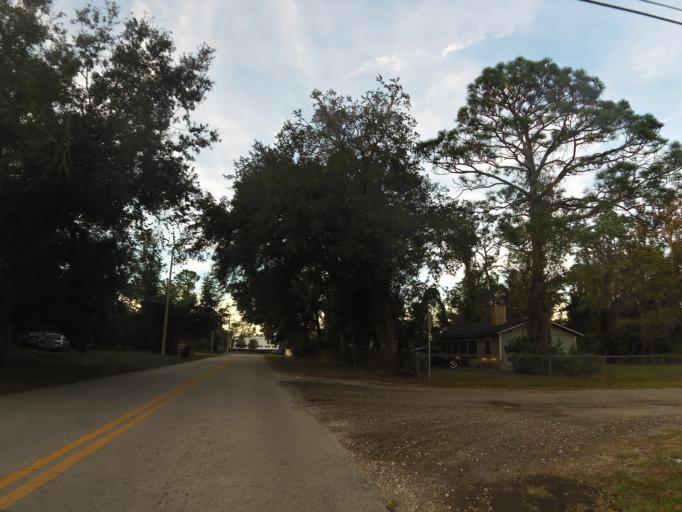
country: US
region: Florida
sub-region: Saint Johns County
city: Fruit Cove
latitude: 30.1603
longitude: -81.5425
